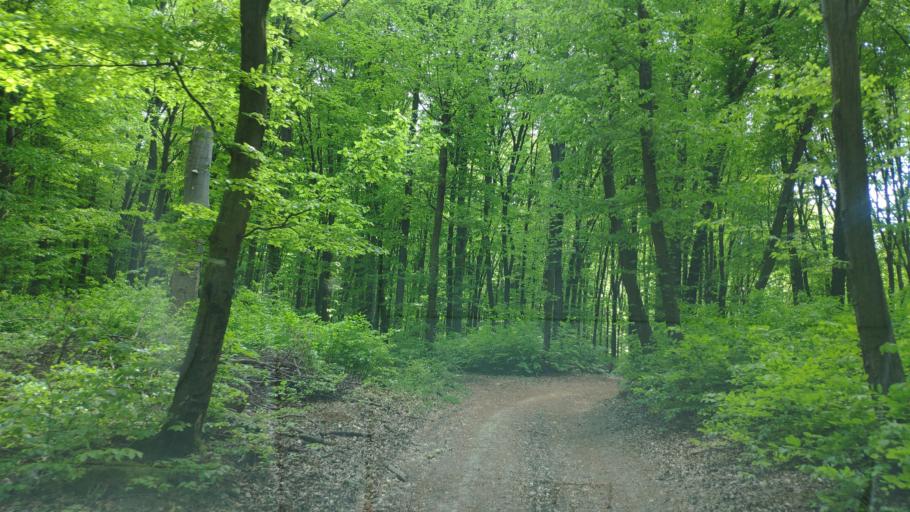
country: SK
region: Kosicky
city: Kosice
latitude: 48.6714
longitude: 21.4345
